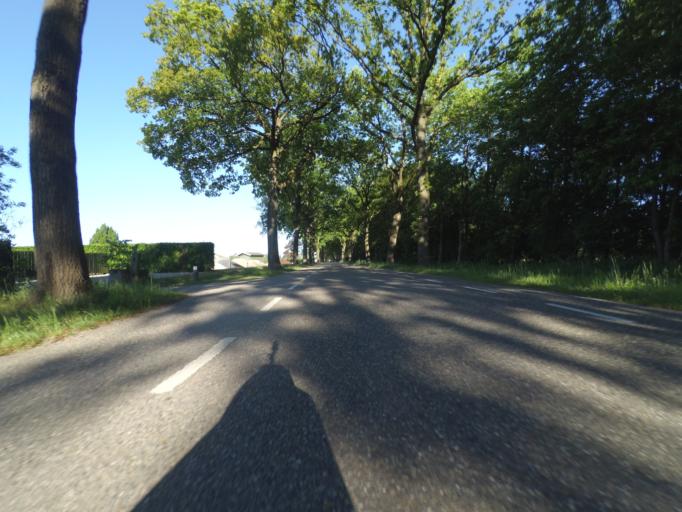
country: NL
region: Gelderland
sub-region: Gemeente Apeldoorn
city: Loenen
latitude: 52.1651
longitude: 6.0165
